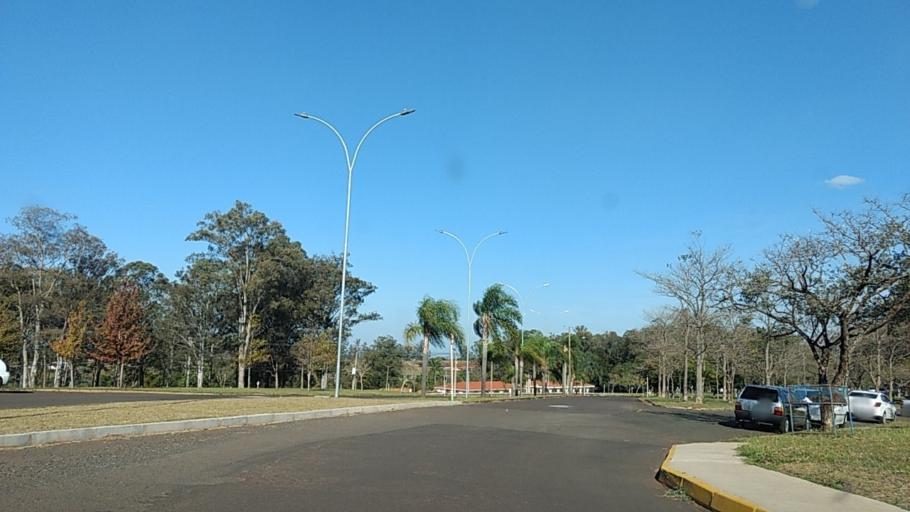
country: BR
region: Sao Paulo
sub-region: Botucatu
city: Botucatu
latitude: -22.8507
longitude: -48.4344
